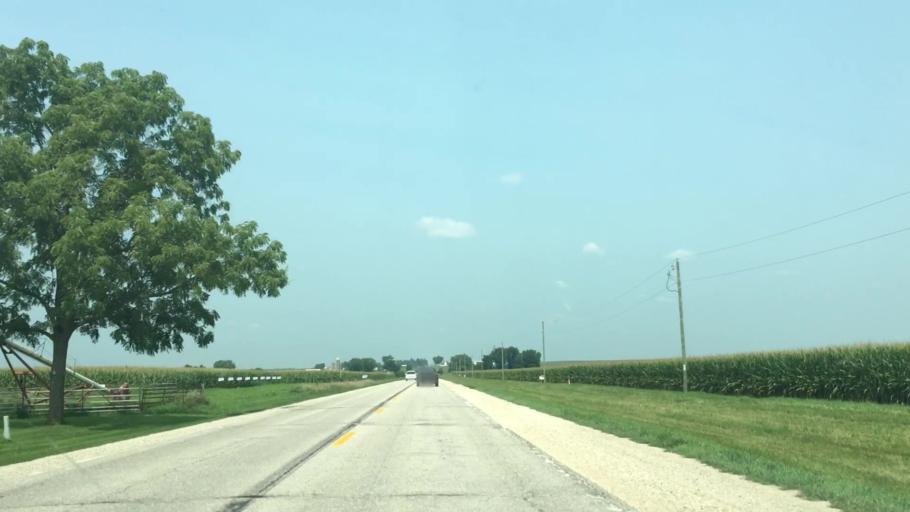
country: US
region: Iowa
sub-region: Benton County
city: Urbana
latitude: 42.3045
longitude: -91.8894
